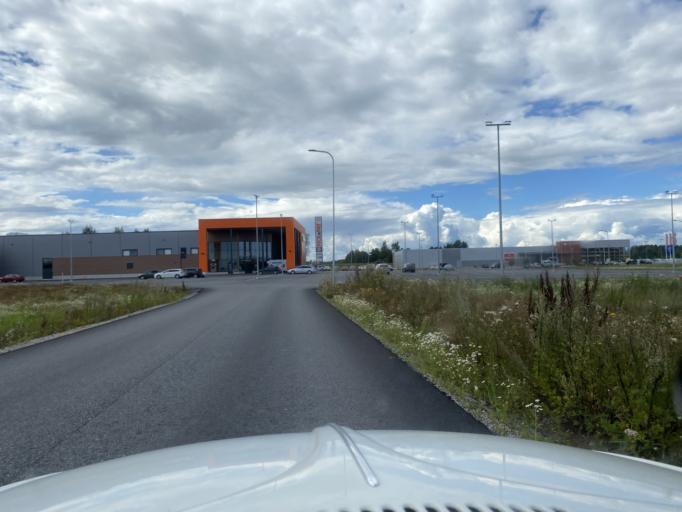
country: FI
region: Satakunta
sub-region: Pori
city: Huittinen
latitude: 61.1699
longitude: 22.6816
